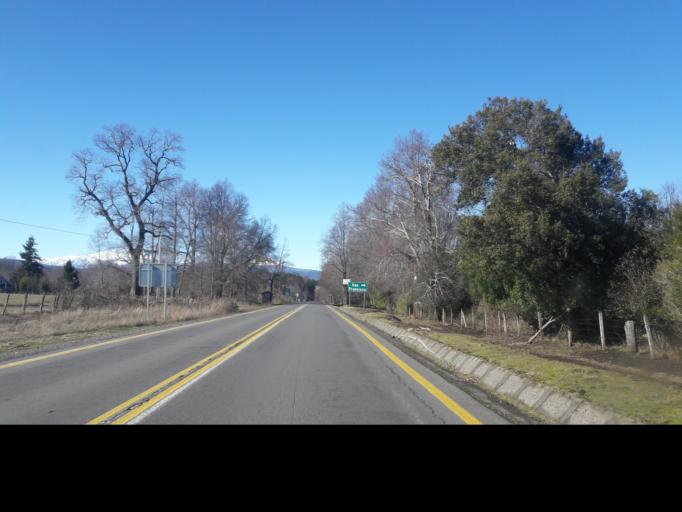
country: CL
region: Araucania
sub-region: Provincia de Malleco
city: Victoria
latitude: -38.3297
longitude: -71.9849
